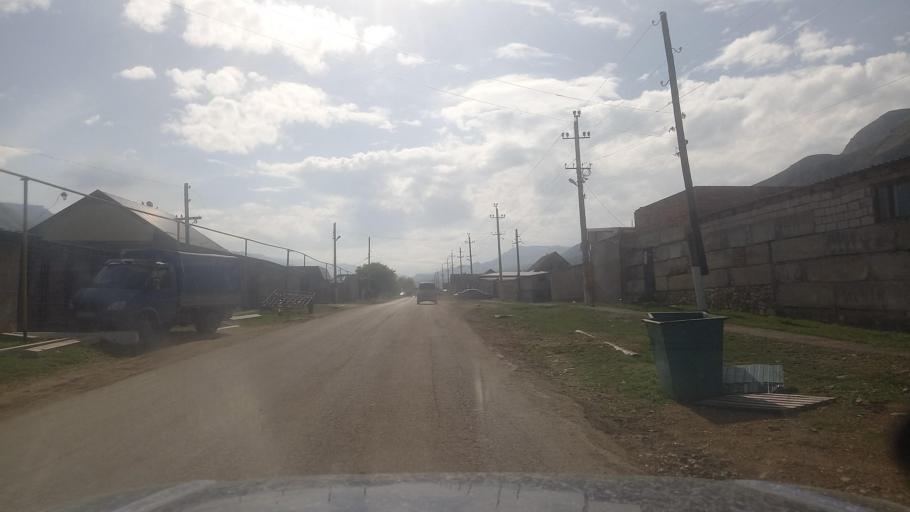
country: RU
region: Kabardino-Balkariya
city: Kamennomostskoye
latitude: 43.7326
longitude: 42.9586
